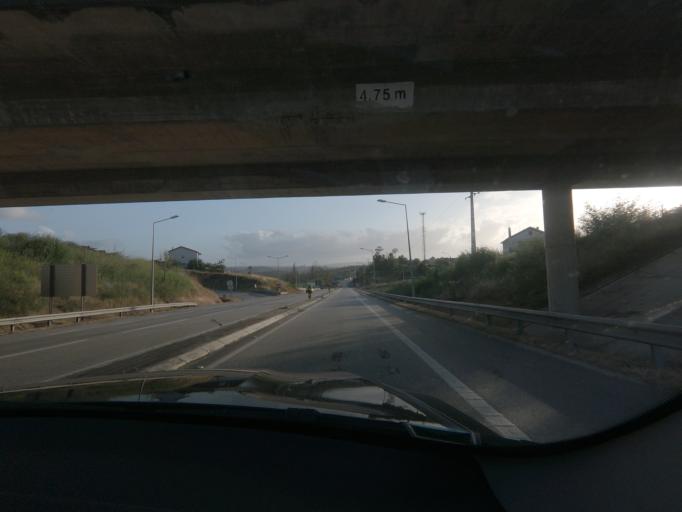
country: PT
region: Viseu
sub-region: Santa Comba Dao
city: Santa Comba Dao
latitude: 40.3542
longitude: -8.1528
